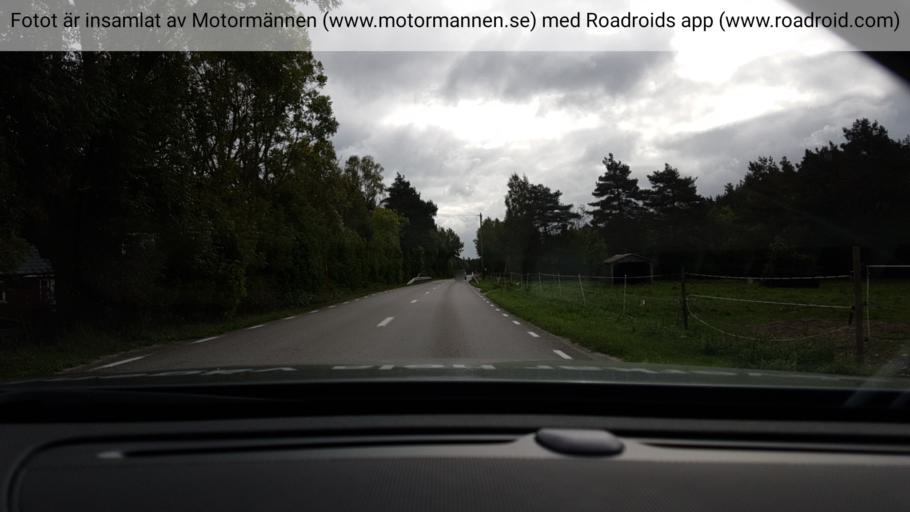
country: SE
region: Gotland
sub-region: Gotland
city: Klintehamn
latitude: 57.2734
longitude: 18.1927
